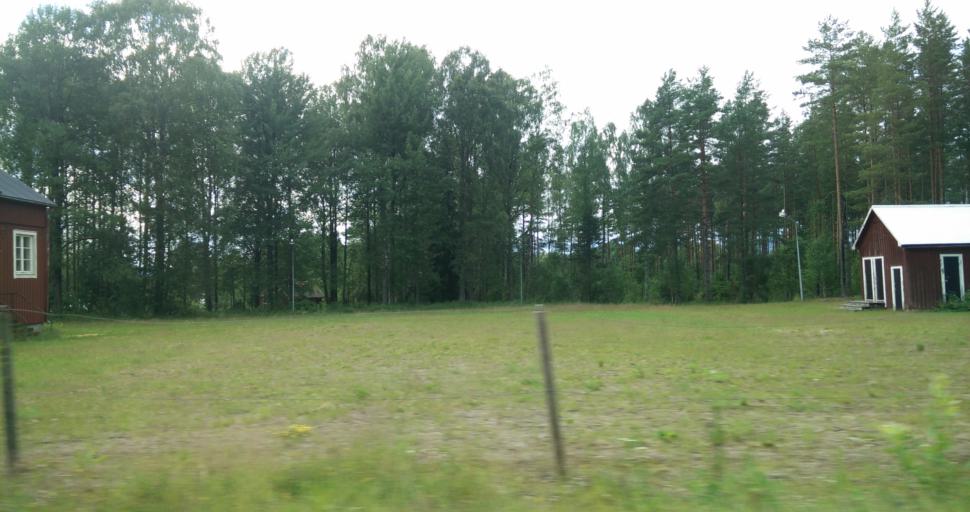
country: SE
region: Vaermland
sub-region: Munkfors Kommun
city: Munkfors
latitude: 59.9804
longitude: 13.4884
